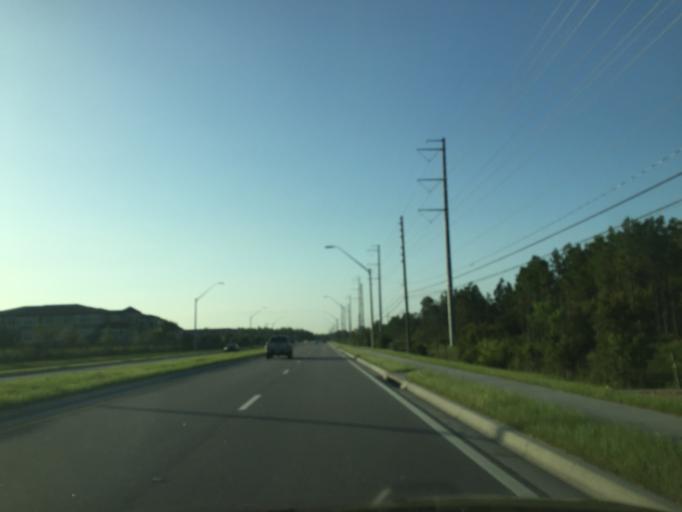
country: US
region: Florida
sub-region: Orange County
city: Alafaya
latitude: 28.5082
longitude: -81.1656
